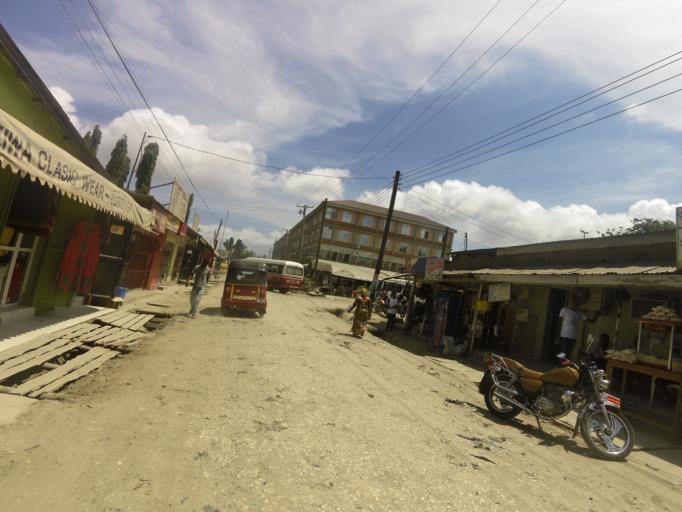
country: TZ
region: Dar es Salaam
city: Magomeni
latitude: -6.7776
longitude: 39.2462
